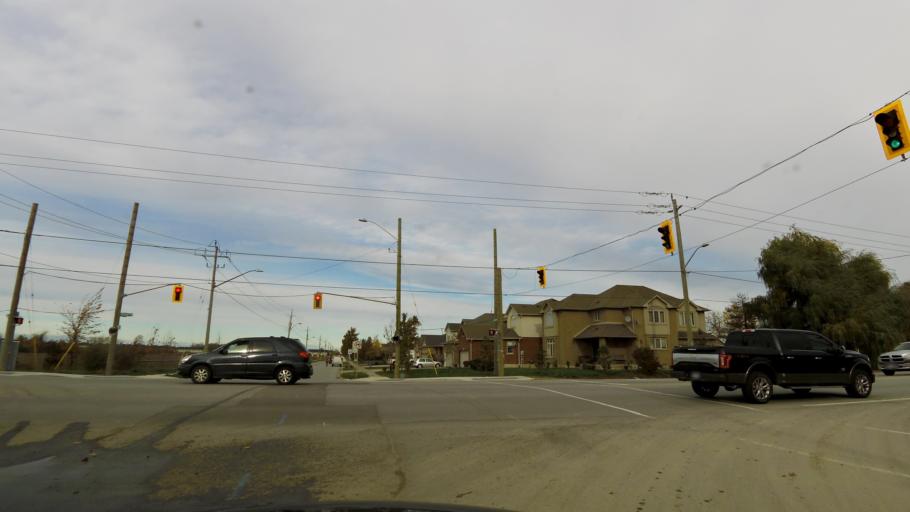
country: CA
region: Ontario
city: Hamilton
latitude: 43.1775
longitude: -79.7960
